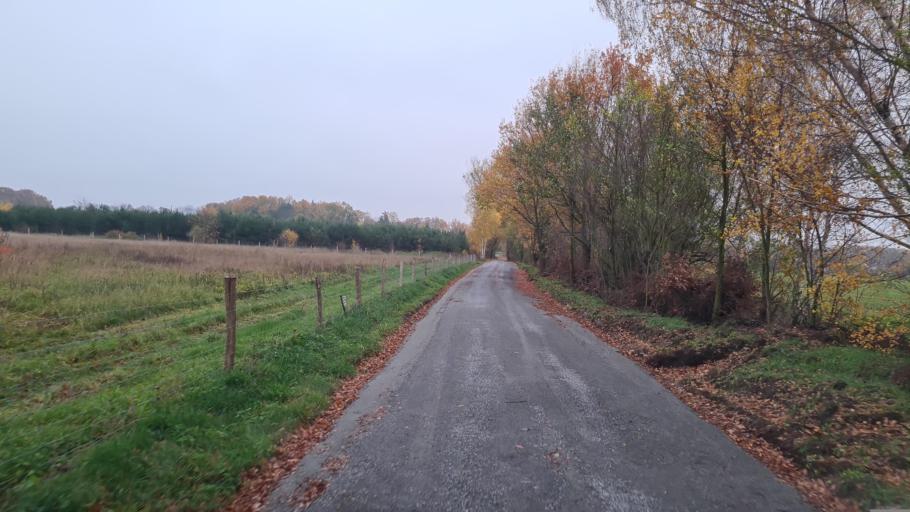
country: DE
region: Brandenburg
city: Kroppen
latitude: 51.3900
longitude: 13.8053
